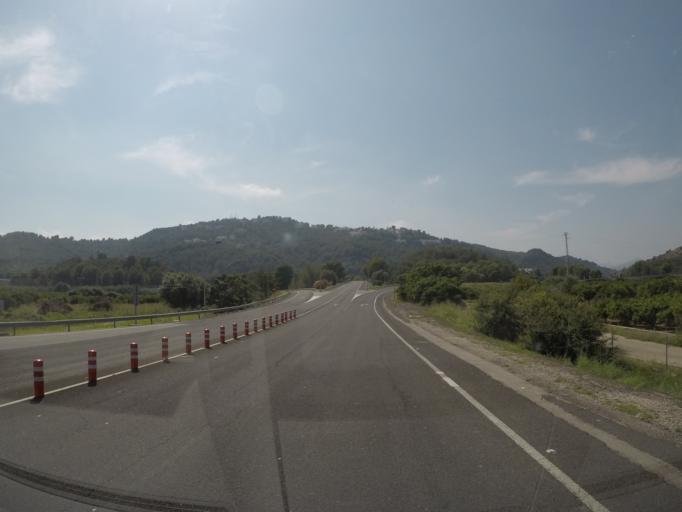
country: ES
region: Valencia
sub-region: Provincia de Valencia
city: L'Alqueria de la Comtessa
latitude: 38.9257
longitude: -0.1378
